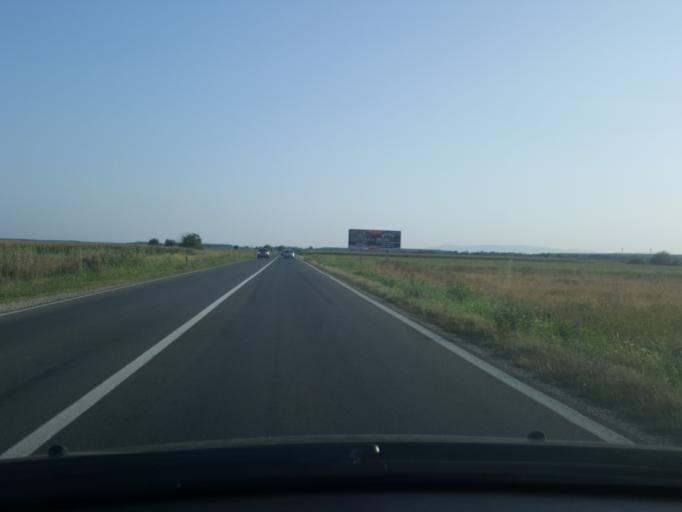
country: RS
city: Klenak
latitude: 44.7972
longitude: 19.7284
